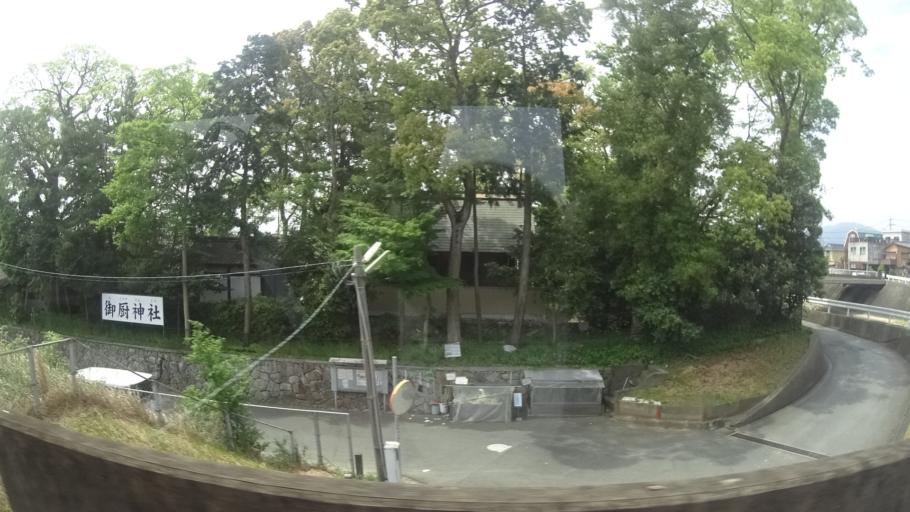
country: JP
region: Mie
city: Hisai-motomachi
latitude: 34.5810
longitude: 136.5318
